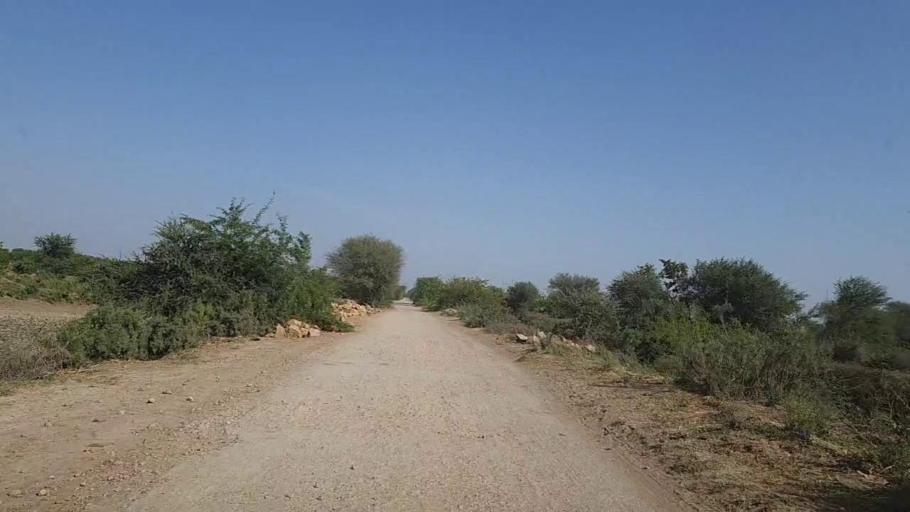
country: PK
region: Sindh
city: Kotri
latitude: 25.1672
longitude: 68.2875
